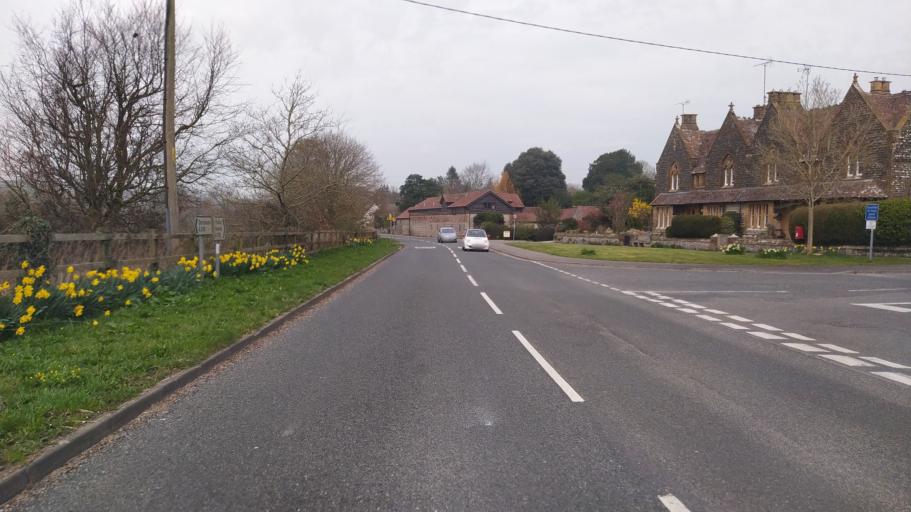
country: GB
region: England
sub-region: Dorset
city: Dorchester
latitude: 50.7529
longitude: -2.5305
